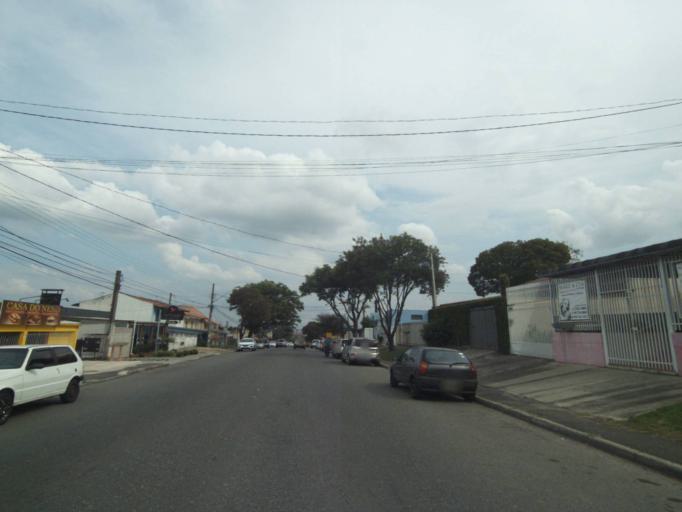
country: BR
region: Parana
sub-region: Pinhais
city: Pinhais
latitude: -25.4170
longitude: -49.2042
